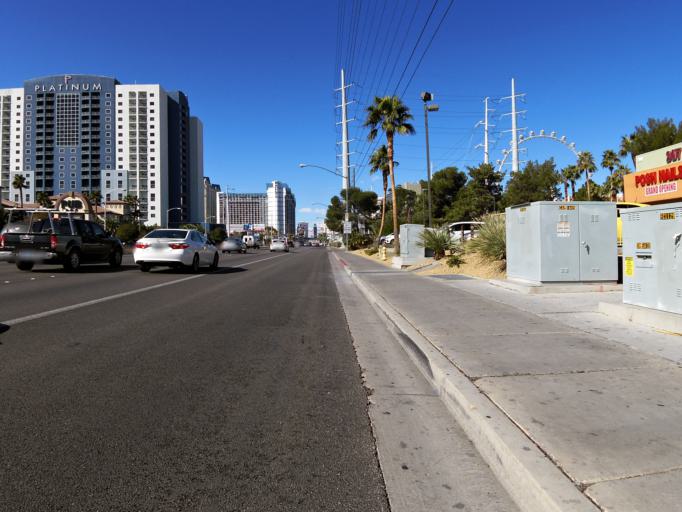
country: US
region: Nevada
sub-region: Clark County
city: Paradise
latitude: 36.1146
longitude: -115.1607
